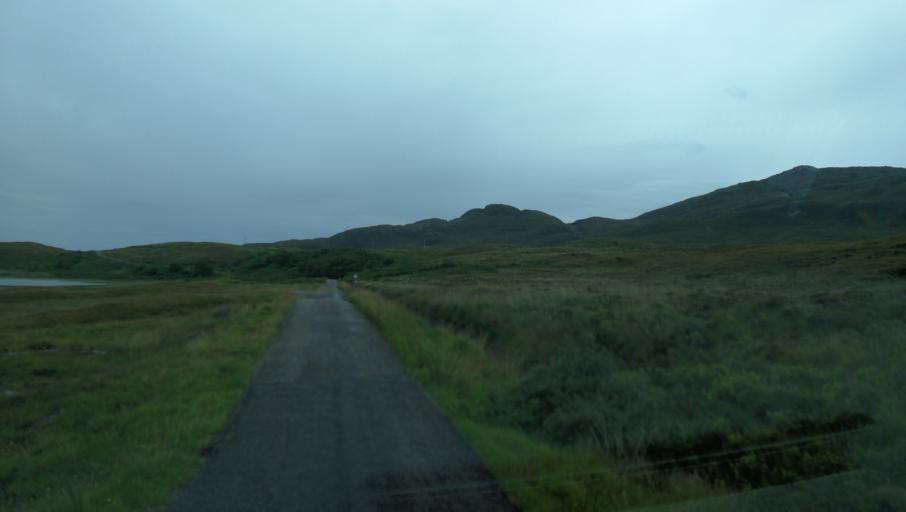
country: GB
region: Scotland
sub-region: Argyll and Bute
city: Isle Of Mull
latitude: 56.7159
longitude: -6.1492
